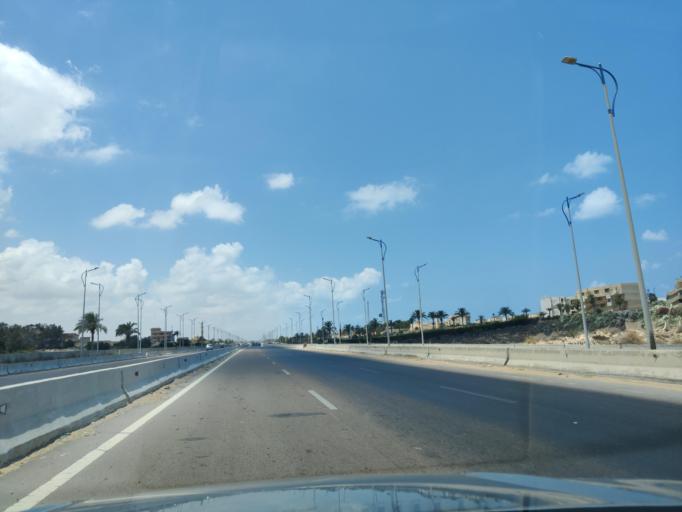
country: EG
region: Muhafazat Matruh
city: Al `Alamayn
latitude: 30.9309
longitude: 29.4785
